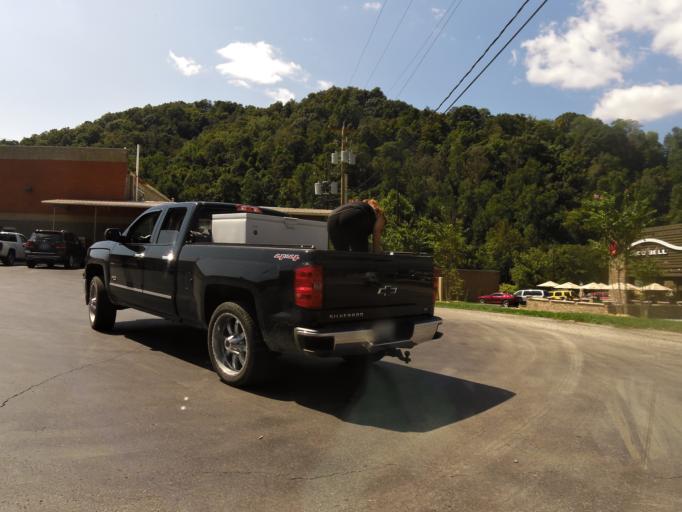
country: US
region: Kentucky
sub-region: Harlan County
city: Harlan
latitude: 36.8201
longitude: -83.3187
